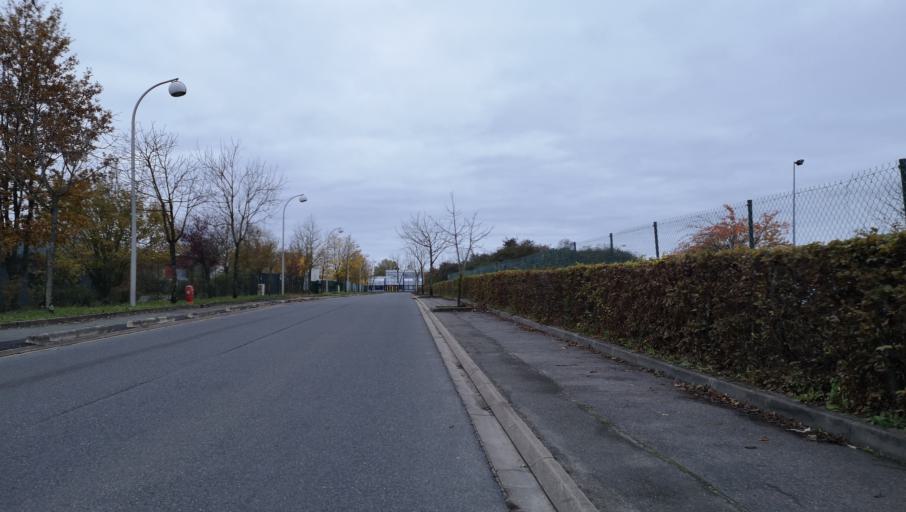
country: FR
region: Centre
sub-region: Departement du Loiret
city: Semoy
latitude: 47.9165
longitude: 1.9458
